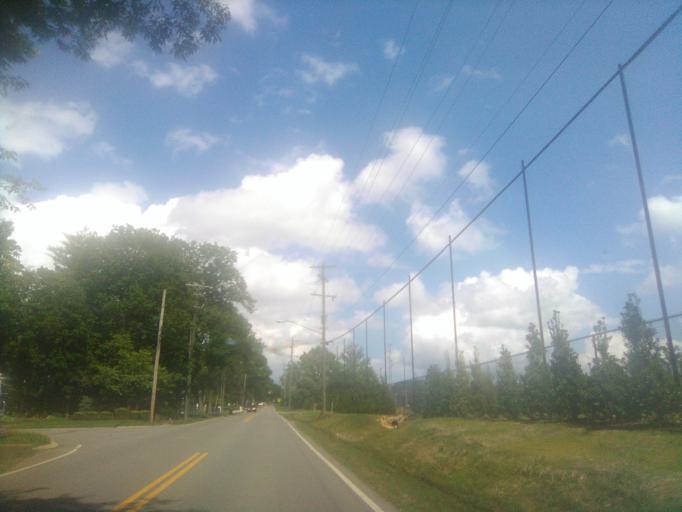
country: US
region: Tennessee
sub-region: Davidson County
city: Belle Meade
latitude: 36.1036
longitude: -86.8437
